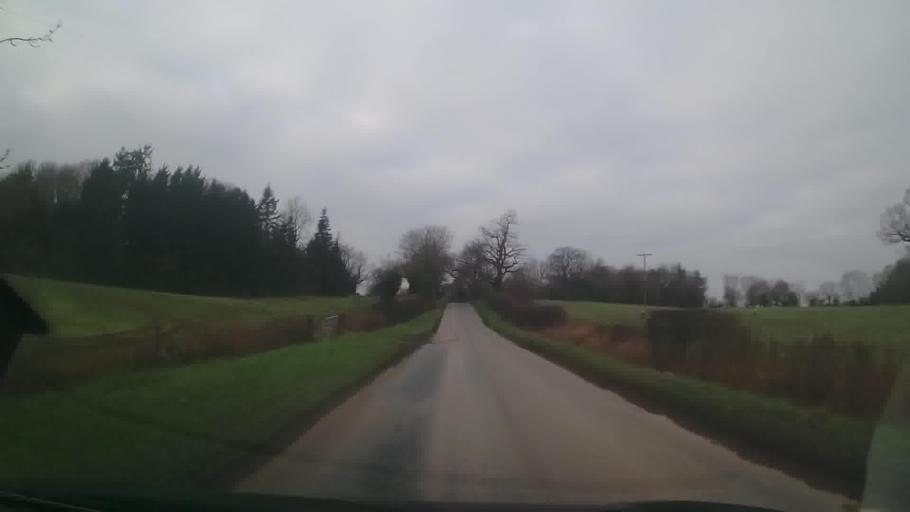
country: GB
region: England
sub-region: Shropshire
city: Bicton
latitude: 52.7590
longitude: -2.8323
